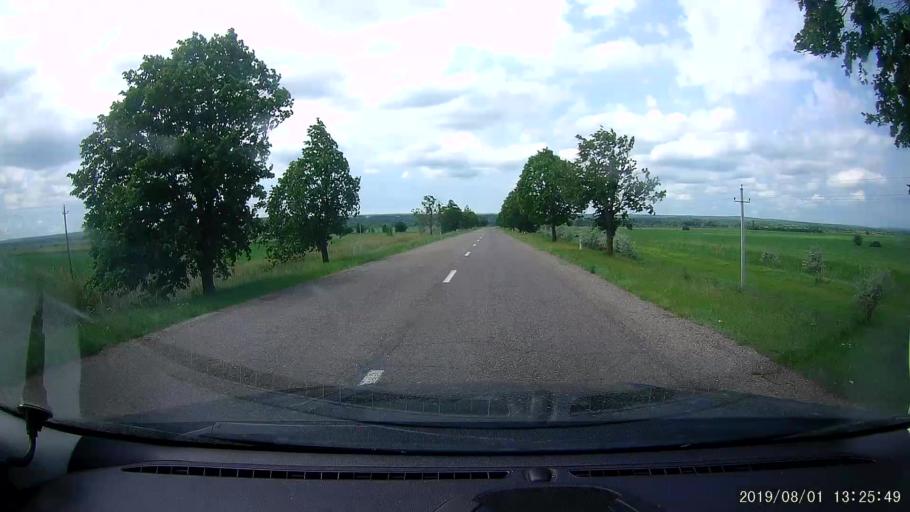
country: RO
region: Galati
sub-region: Comuna Oancea
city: Oancea
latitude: 45.9144
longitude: 28.1449
